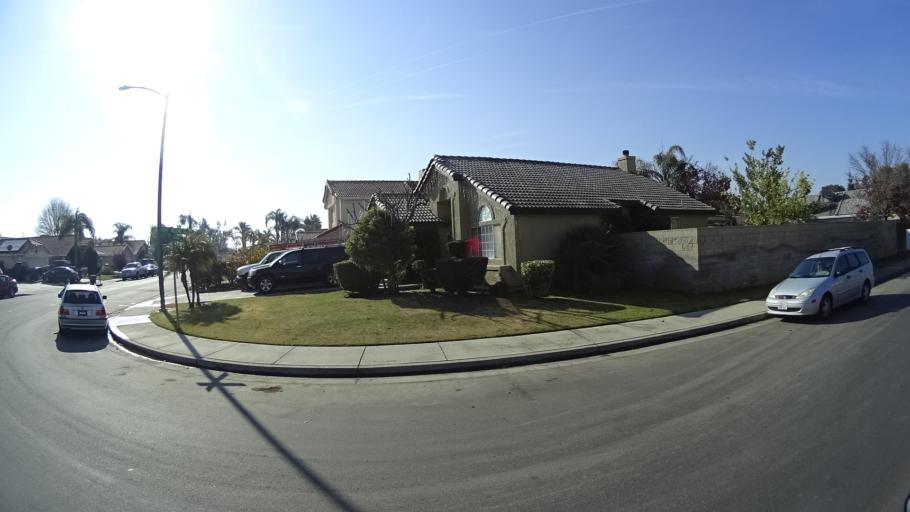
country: US
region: California
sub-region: Kern County
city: Greenfield
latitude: 35.3120
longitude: -119.0229
